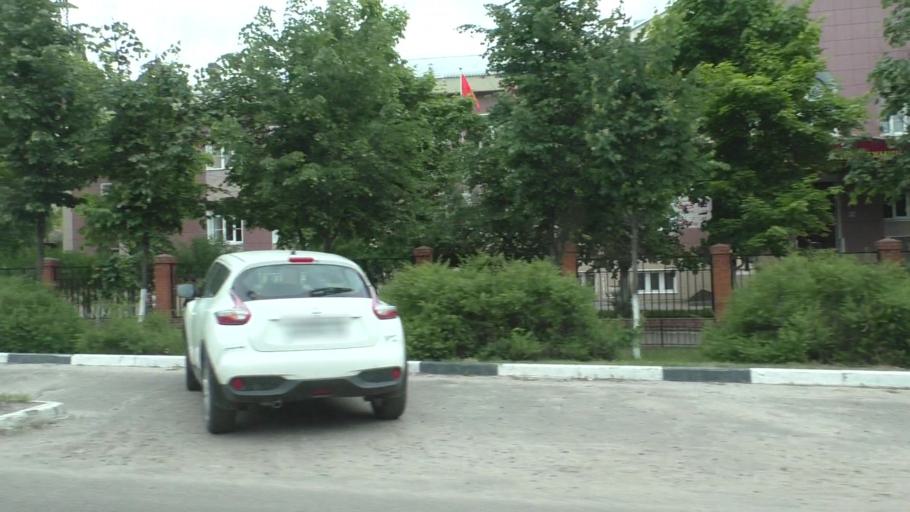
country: RU
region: Moskovskaya
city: Yegor'yevsk
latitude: 55.3732
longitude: 39.0532
